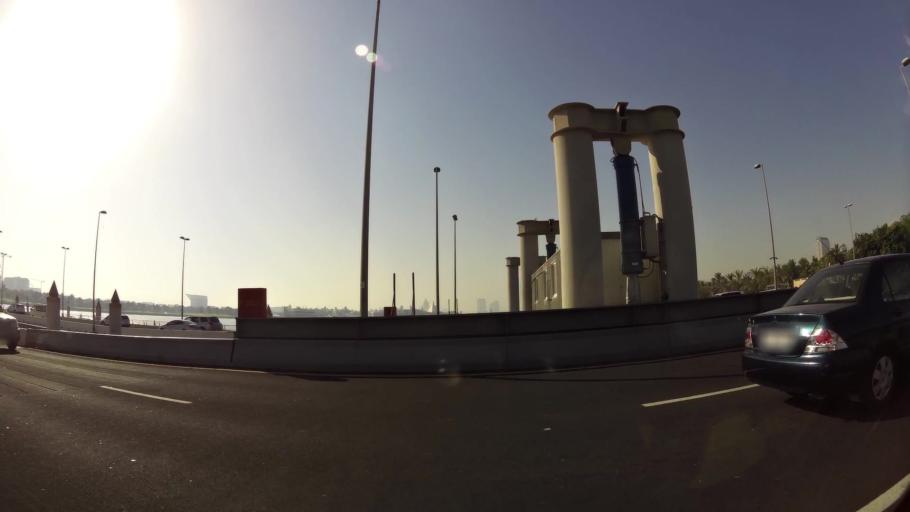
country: AE
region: Ash Shariqah
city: Sharjah
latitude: 25.2481
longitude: 55.3247
